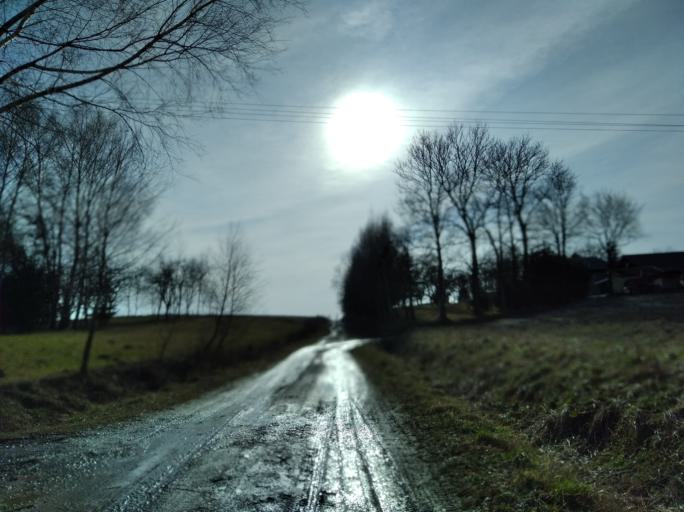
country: PL
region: Subcarpathian Voivodeship
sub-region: Powiat brzozowski
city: Gorki
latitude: 49.6530
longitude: 22.0469
